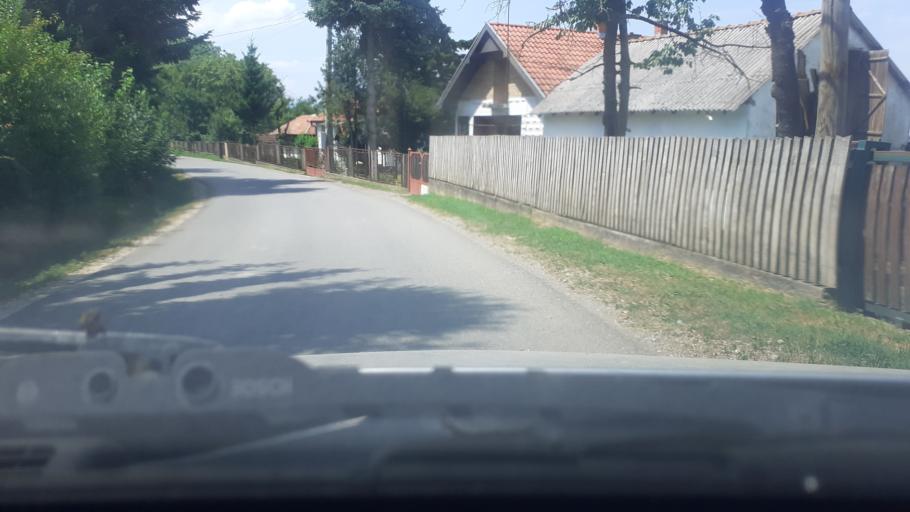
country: RS
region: Central Serbia
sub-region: Kolubarski Okrug
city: Osecina
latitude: 44.3939
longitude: 19.4935
